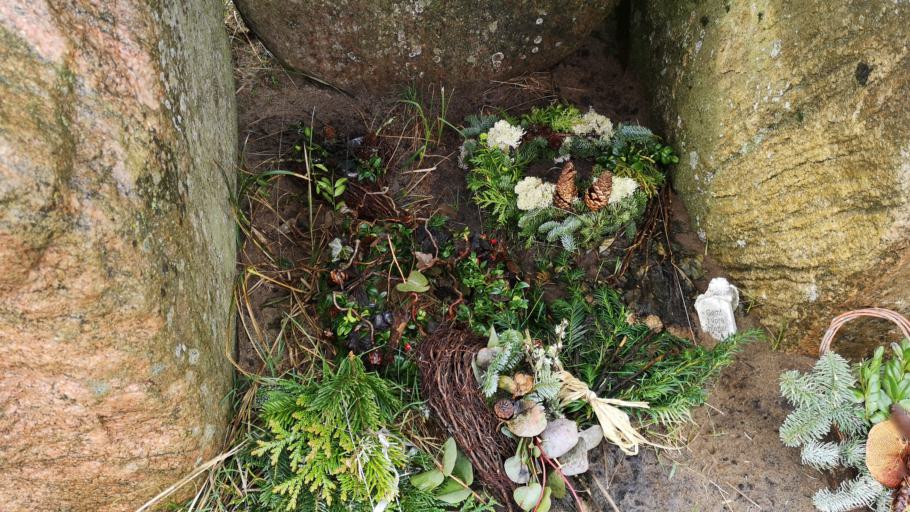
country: DK
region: Central Jutland
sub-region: Ikast-Brande Kommune
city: Brande
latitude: 56.0244
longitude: 9.1456
